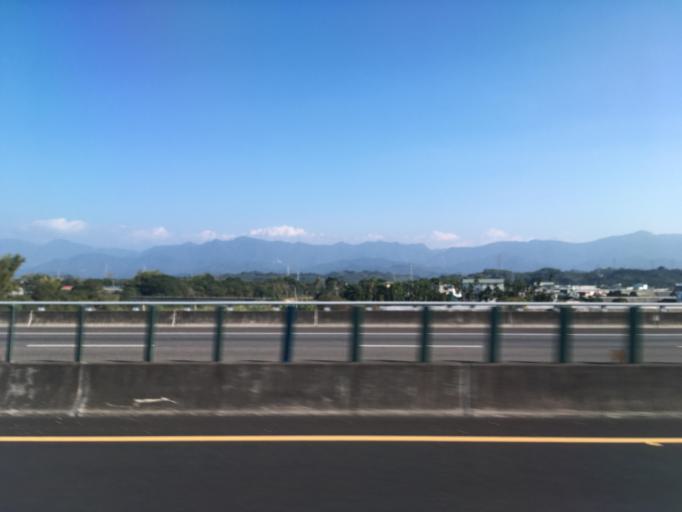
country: TW
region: Taiwan
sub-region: Chiayi
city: Jiayi Shi
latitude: 23.4403
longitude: 120.4798
